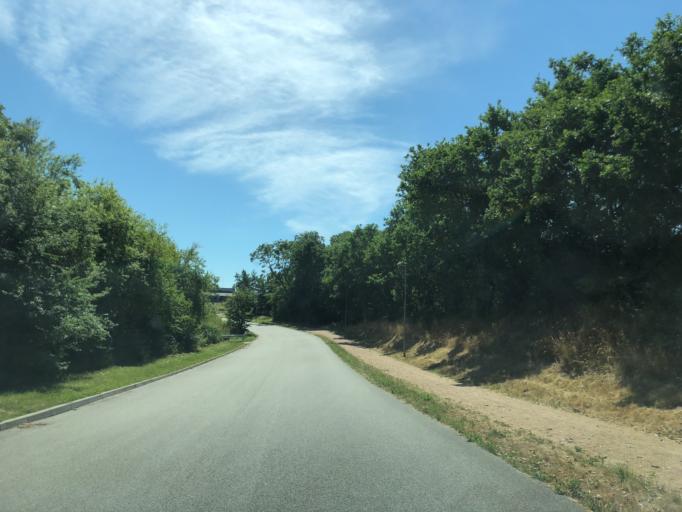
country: DK
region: Central Jutland
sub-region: Skive Kommune
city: Skive
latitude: 56.5478
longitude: 9.0133
